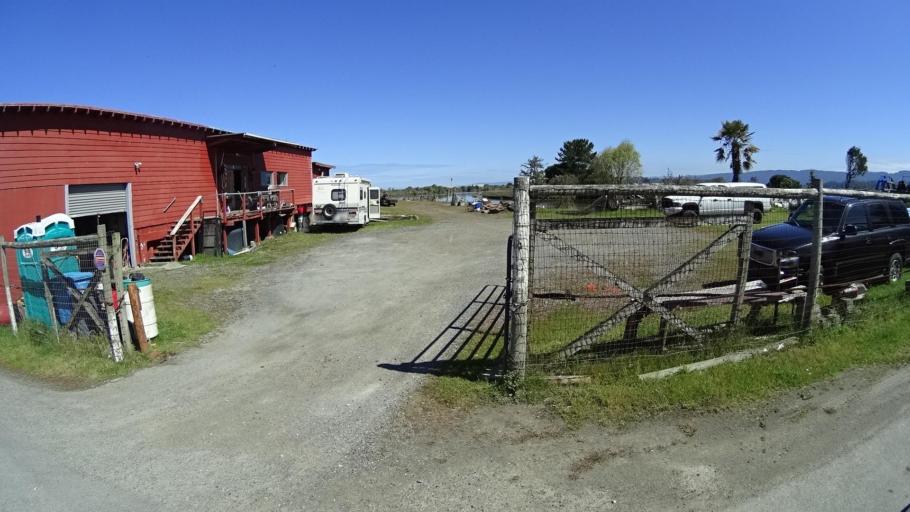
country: US
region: California
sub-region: Humboldt County
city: Myrtletown
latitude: 40.7952
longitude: -124.1213
